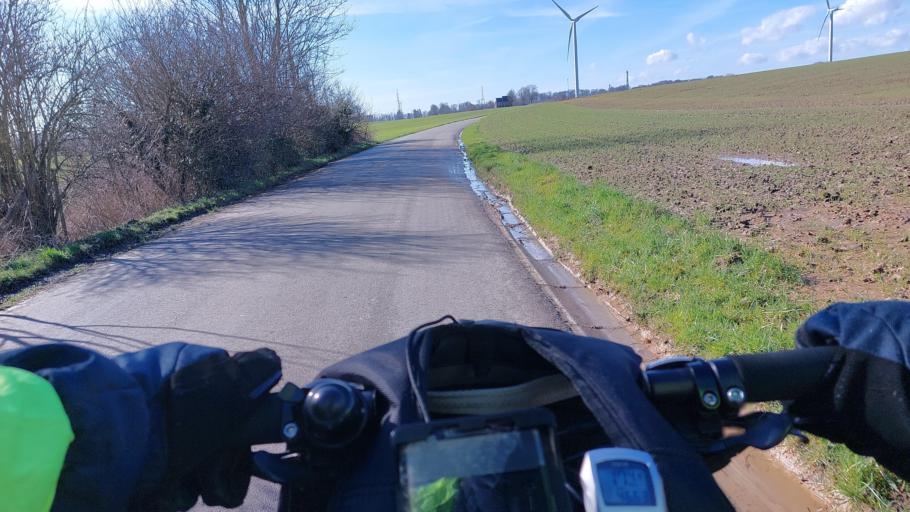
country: BE
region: Wallonia
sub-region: Province du Hainaut
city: Seneffe
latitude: 50.5623
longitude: 4.2407
